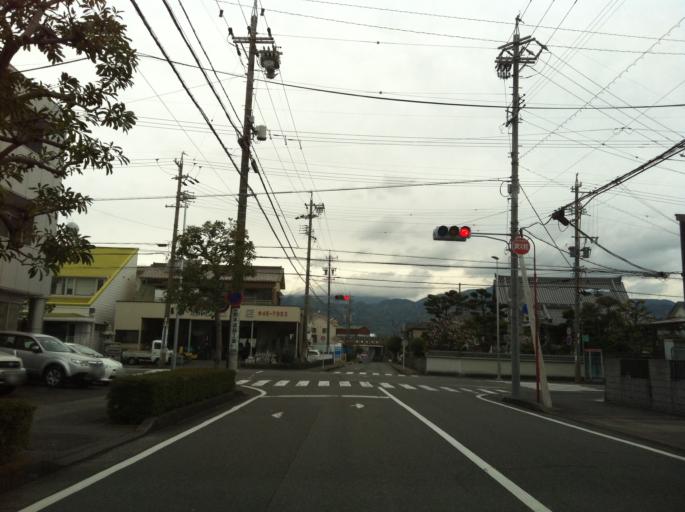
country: JP
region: Shizuoka
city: Shizuoka-shi
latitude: 35.0200
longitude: 138.4681
